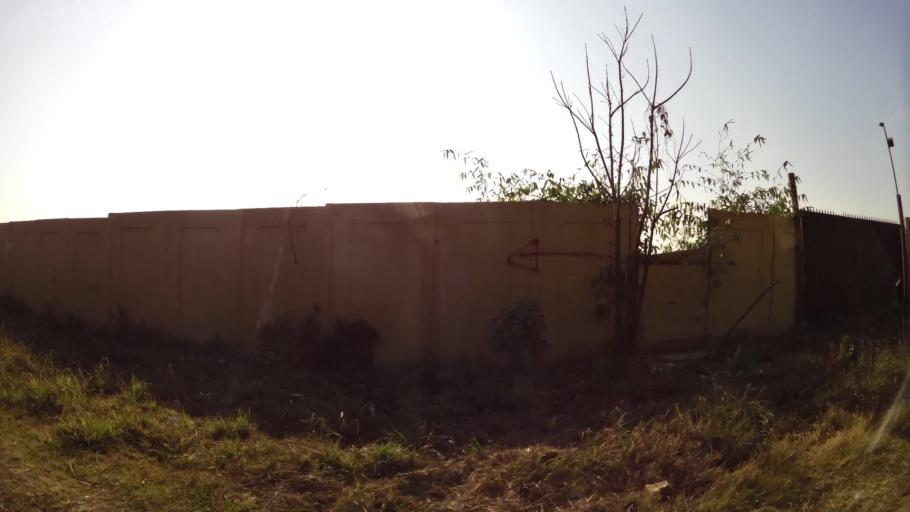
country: ZA
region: Gauteng
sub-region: City of Tshwane Metropolitan Municipality
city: Pretoria
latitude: -25.7588
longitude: 28.3383
